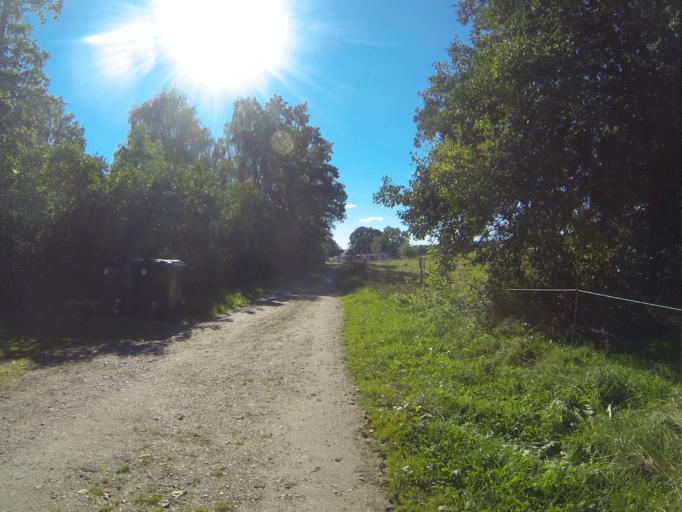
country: SE
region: Skane
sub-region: Hoors Kommun
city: Loberod
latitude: 55.7221
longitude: 13.4069
